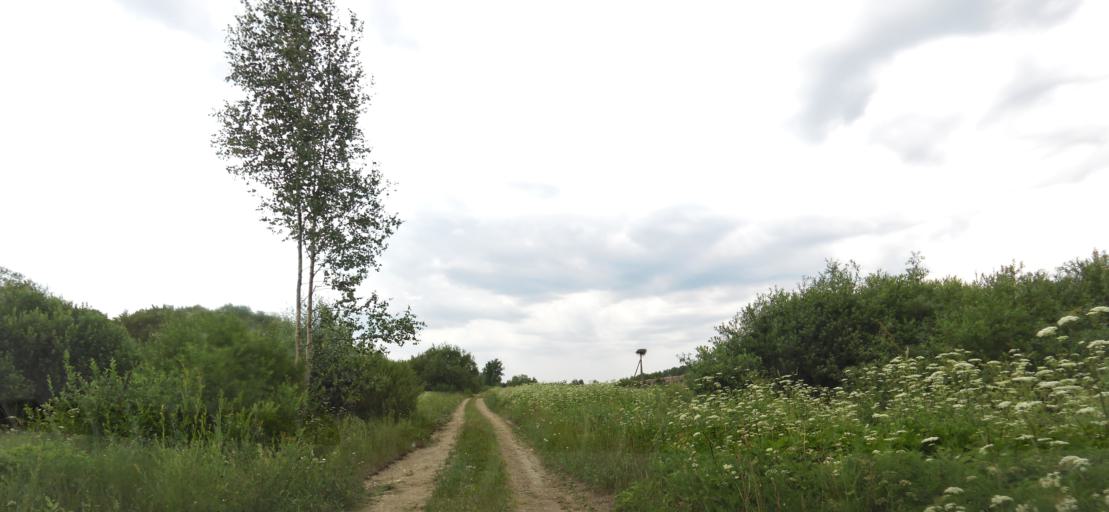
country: LT
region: Panevezys
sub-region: Birzai
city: Birzai
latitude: 56.3595
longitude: 24.9680
